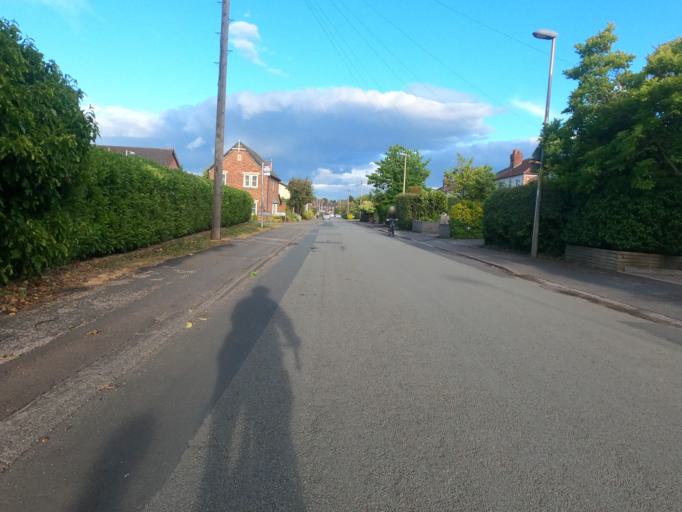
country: GB
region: England
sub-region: Cheshire West and Chester
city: Northwich
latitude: 53.2354
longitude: -2.5240
